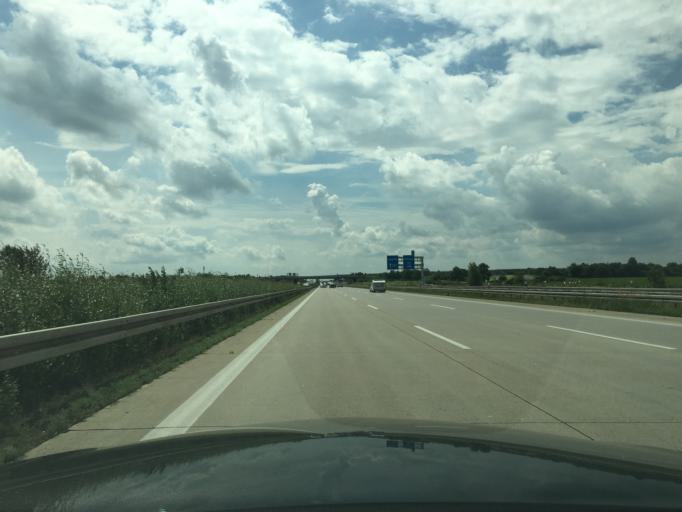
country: DE
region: Saxony-Anhalt
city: Grosskorbetha
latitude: 51.2415
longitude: 12.0636
